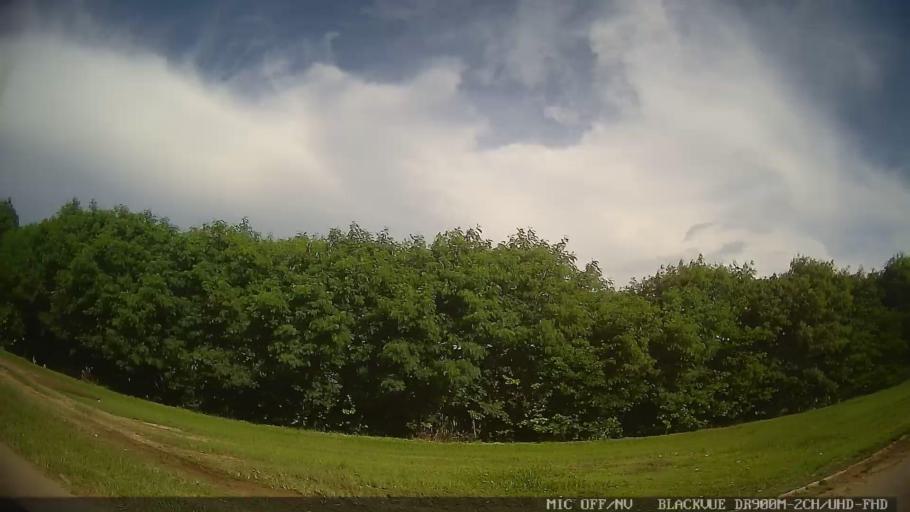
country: BR
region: Sao Paulo
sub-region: Tiete
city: Tiete
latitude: -23.1001
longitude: -47.6910
